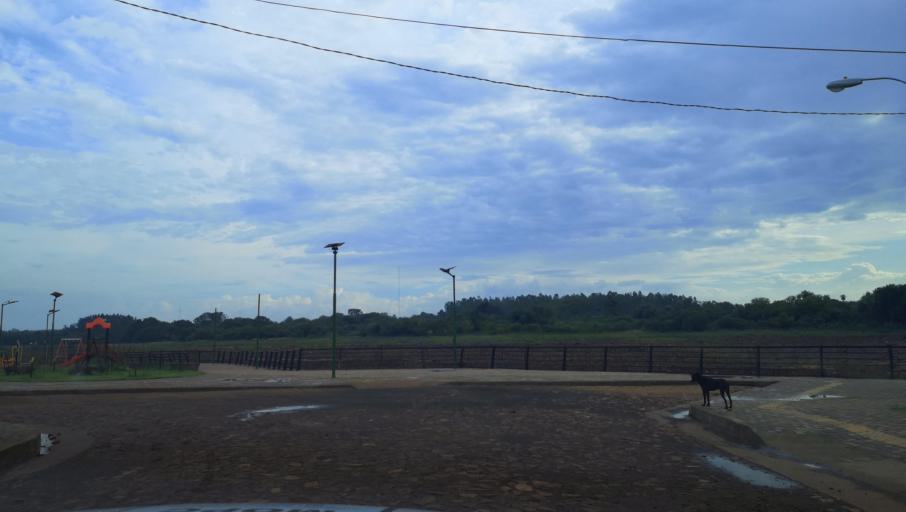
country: PY
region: Misiones
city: Santa Maria
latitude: -26.8817
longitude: -57.0189
